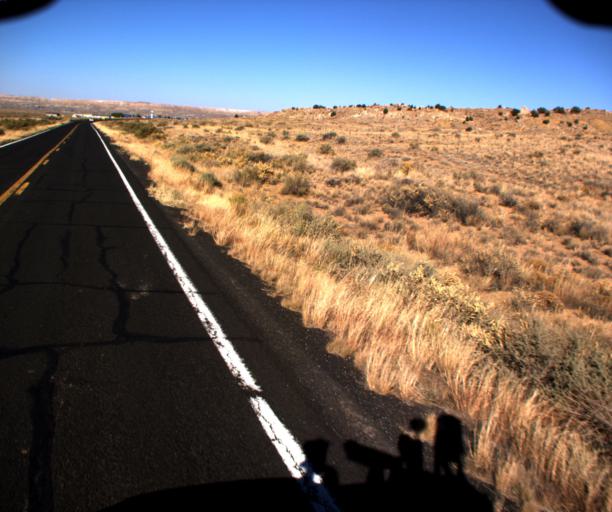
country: US
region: Arizona
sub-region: Navajo County
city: First Mesa
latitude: 35.8302
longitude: -110.2866
